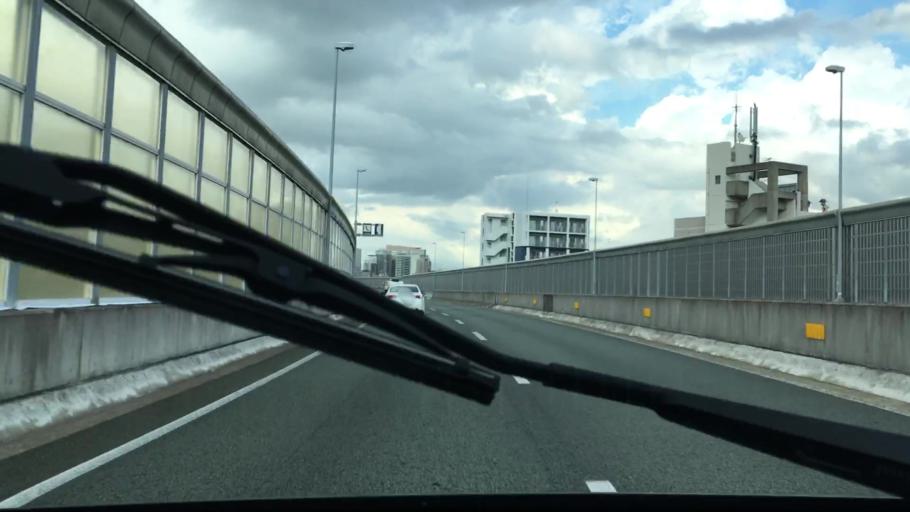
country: JP
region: Fukuoka
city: Fukuoka-shi
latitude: 33.5816
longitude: 130.3365
